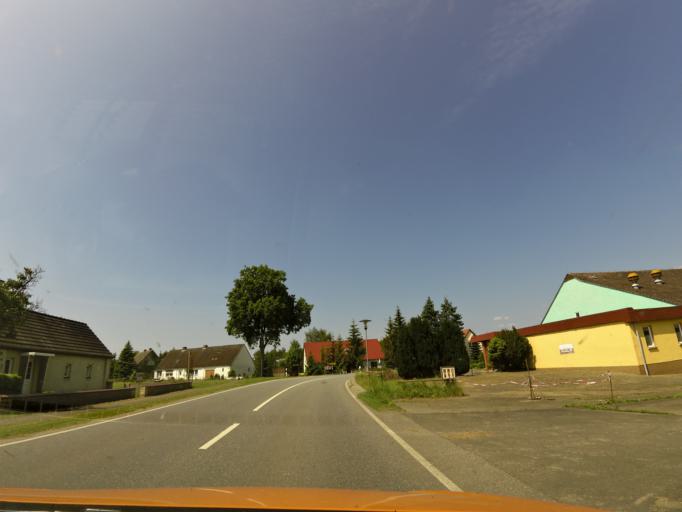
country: DE
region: Mecklenburg-Vorpommern
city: Domsuhl
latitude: 53.5275
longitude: 11.7492
